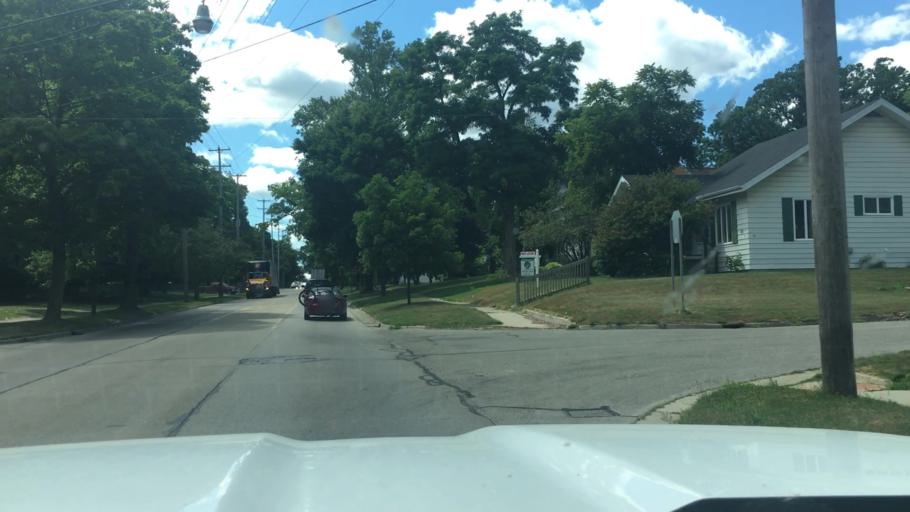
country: US
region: Michigan
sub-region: Montcalm County
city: Greenville
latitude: 43.1775
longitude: -85.2615
